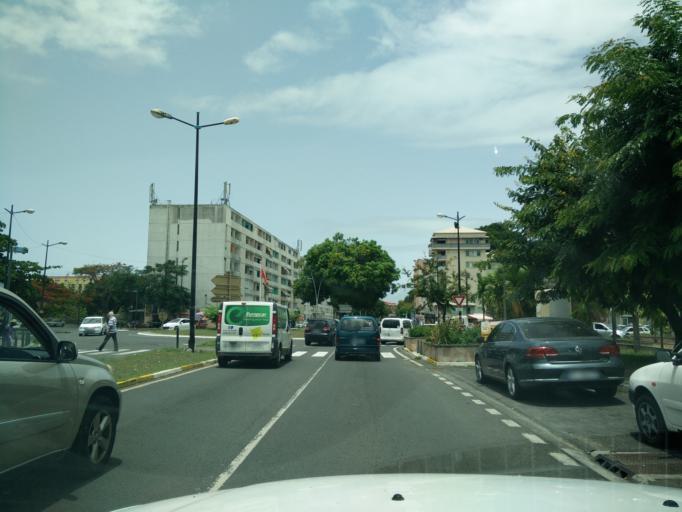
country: GP
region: Guadeloupe
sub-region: Guadeloupe
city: Pointe-a-Pitre
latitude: 16.2433
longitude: -61.5308
